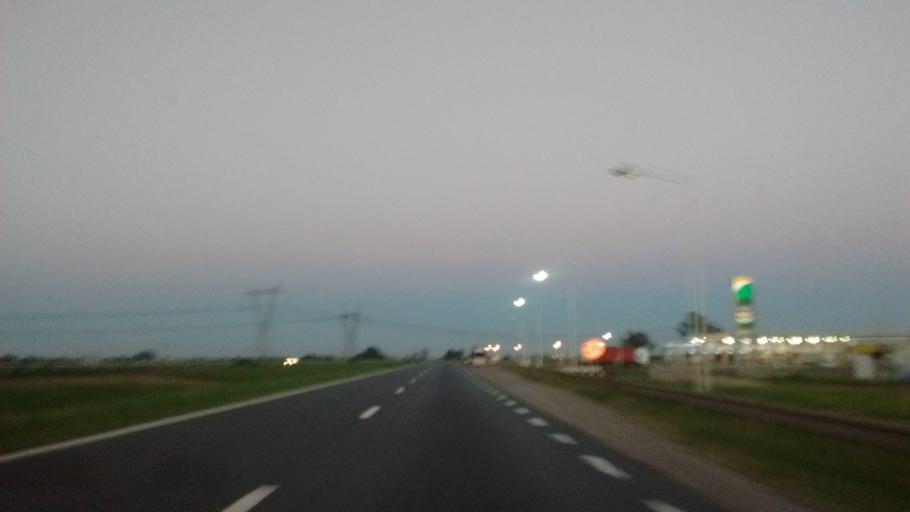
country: AR
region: Santa Fe
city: Roldan
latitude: -32.9249
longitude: -60.9099
